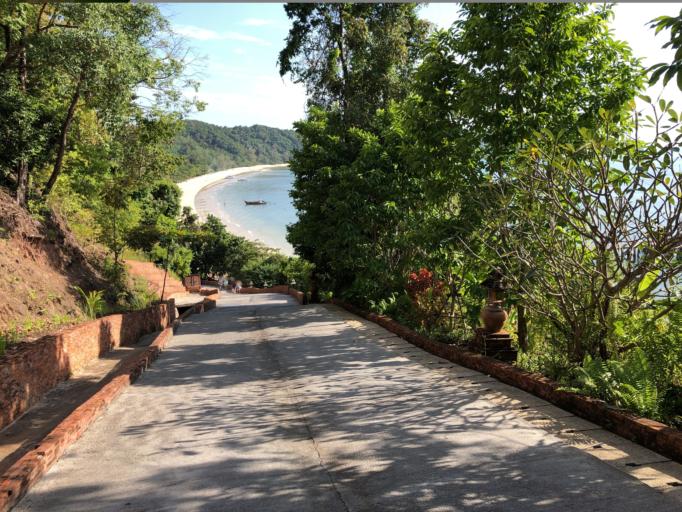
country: TH
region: Phangnga
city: Ban Phru Nai
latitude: 7.9836
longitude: 98.5676
